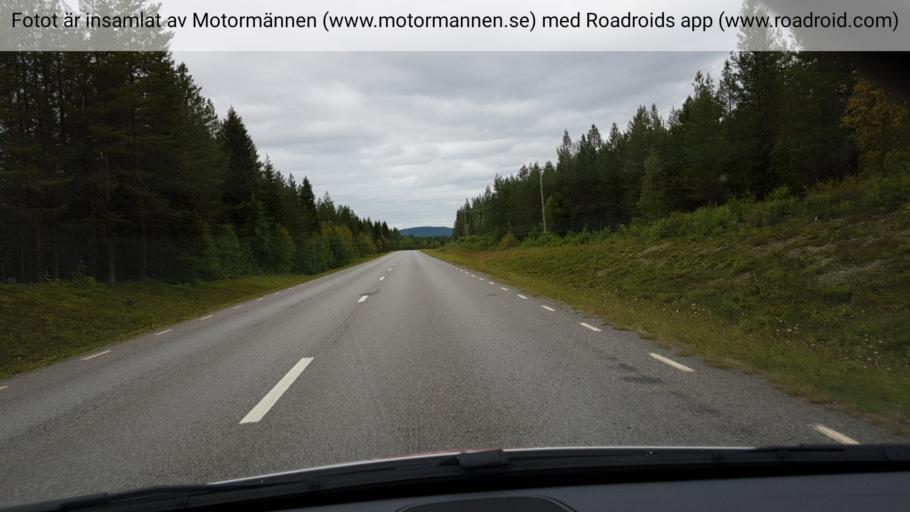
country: SE
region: Jaemtland
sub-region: Stroemsunds Kommun
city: Stroemsund
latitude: 64.2803
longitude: 15.3640
